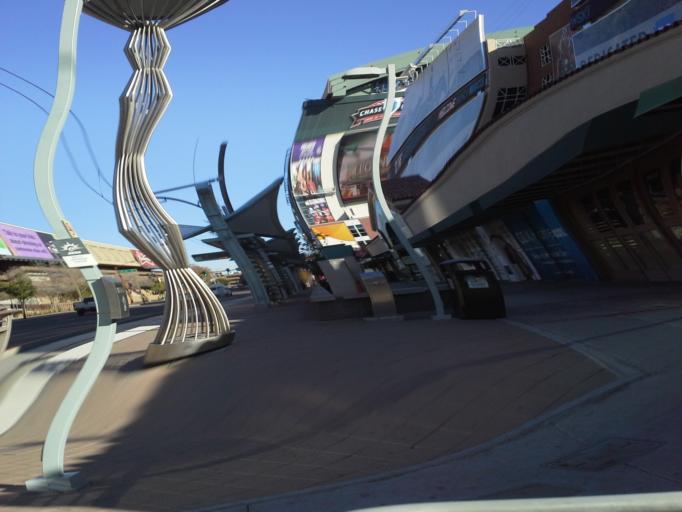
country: US
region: Arizona
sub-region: Maricopa County
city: Phoenix
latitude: 33.4463
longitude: -112.0699
